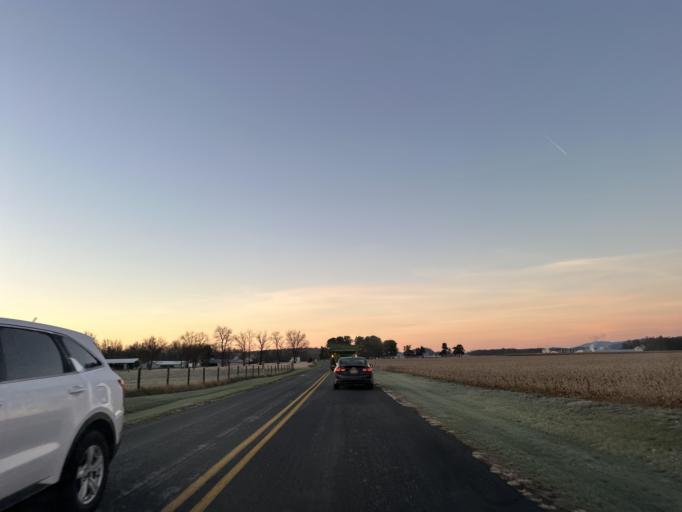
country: US
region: Virginia
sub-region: Rockingham County
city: Bridgewater
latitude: 38.3841
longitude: -79.0780
